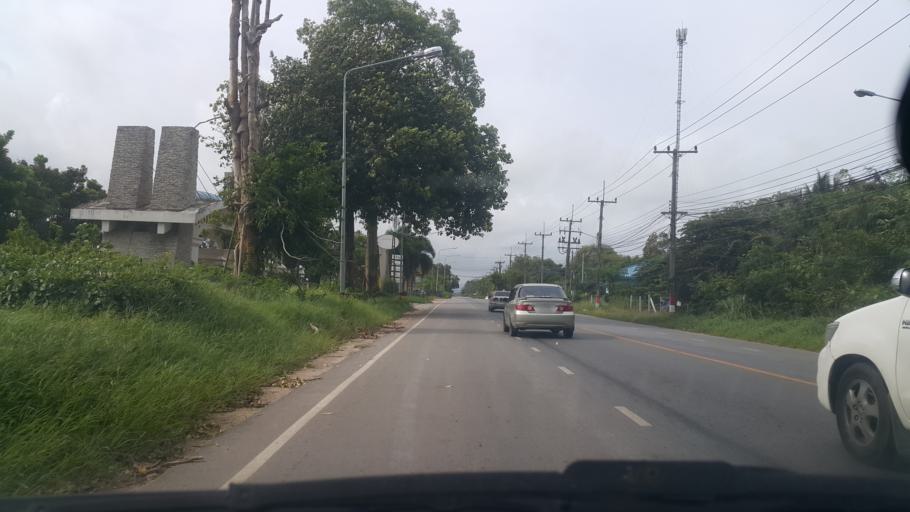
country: TH
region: Rayong
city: Rayong
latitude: 12.6361
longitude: 101.3420
